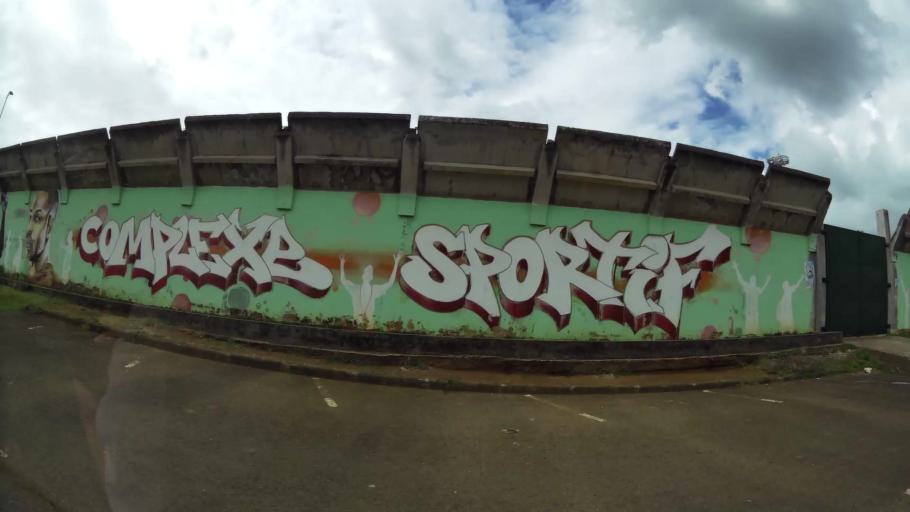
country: GP
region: Guadeloupe
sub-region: Guadeloupe
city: Baie-Mahault
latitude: 16.2632
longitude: -61.5891
